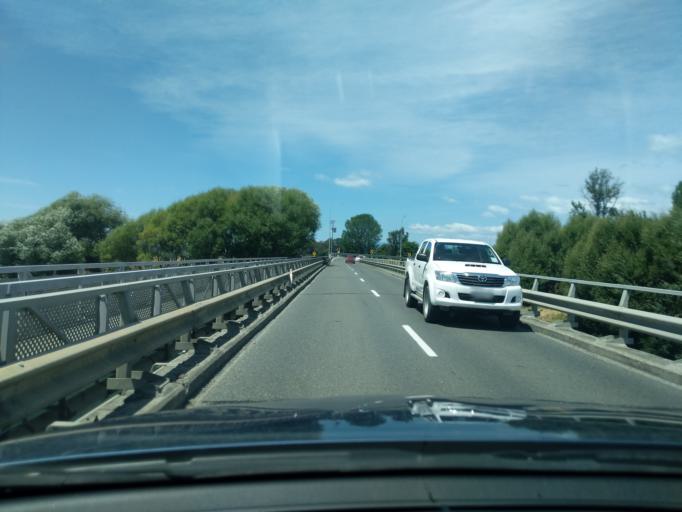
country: NZ
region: Tasman
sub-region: Tasman District
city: Motueka
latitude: -41.0913
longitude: 173.0106
